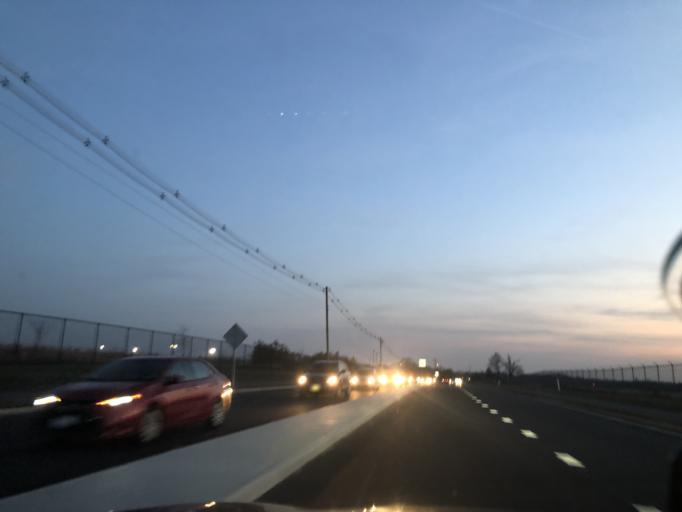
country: US
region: Virginia
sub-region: Loudoun County
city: Leesburg
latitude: 39.0738
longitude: -77.5527
